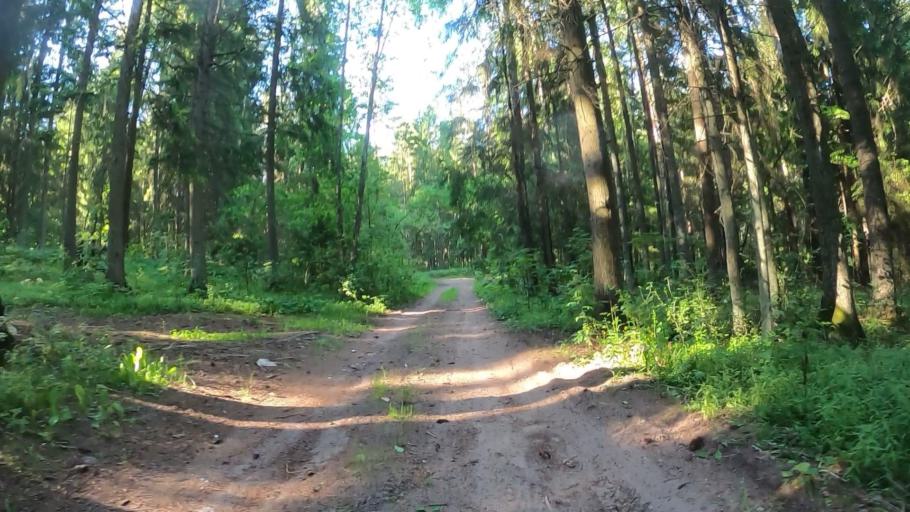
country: LV
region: Ogre
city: Ogre
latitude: 56.8305
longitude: 24.5961
